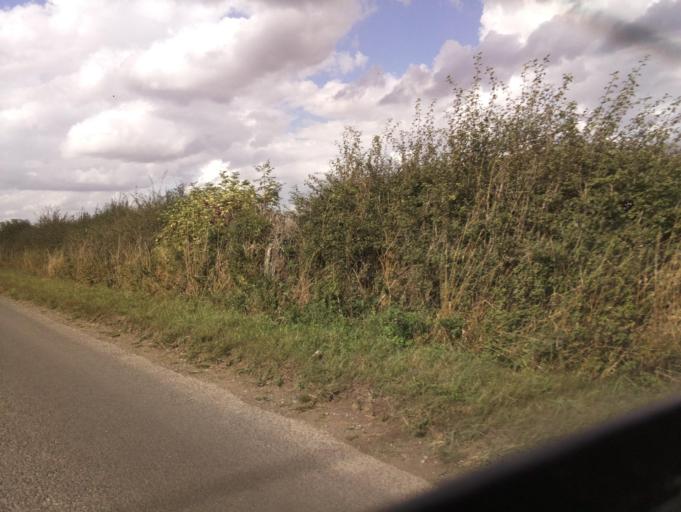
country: GB
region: England
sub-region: North Yorkshire
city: Ripon
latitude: 54.1642
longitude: -1.5474
